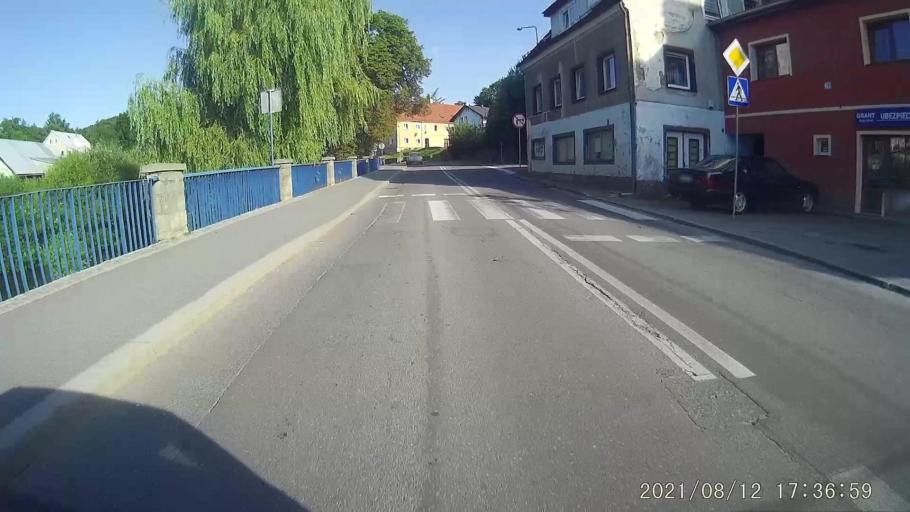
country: PL
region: Lower Silesian Voivodeship
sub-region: Powiat klodzki
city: Ladek-Zdroj
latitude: 50.3436
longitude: 16.8796
